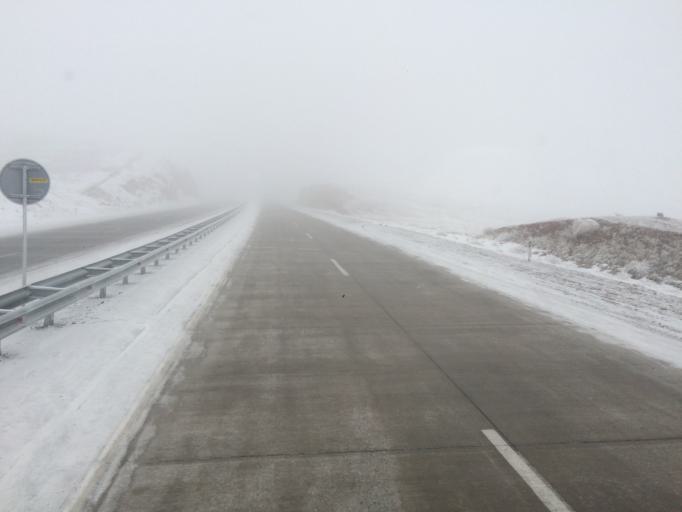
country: KZ
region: Zhambyl
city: Georgiyevka
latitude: 43.4216
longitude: 74.9688
